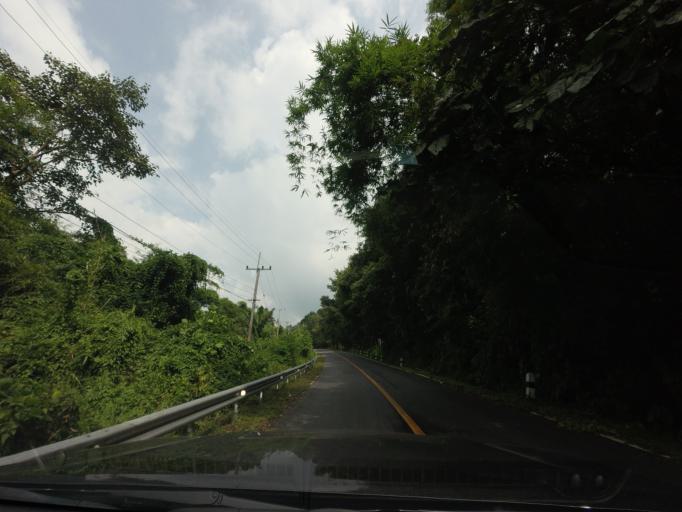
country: TH
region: Nan
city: Pua
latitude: 19.1854
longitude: 101.0103
